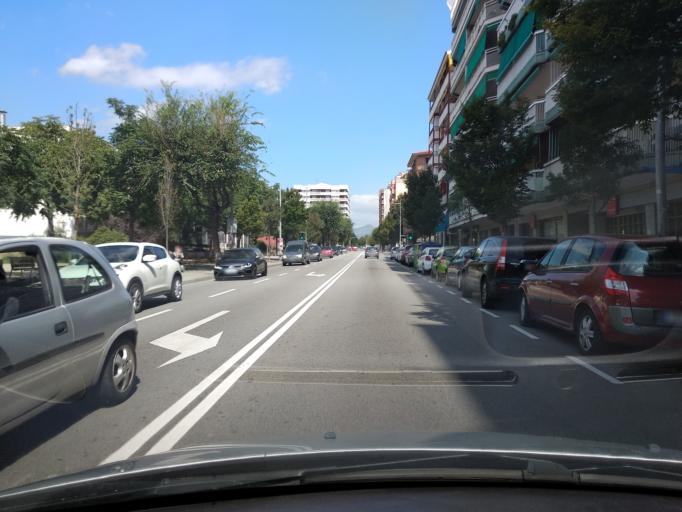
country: ES
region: Catalonia
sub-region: Provincia de Barcelona
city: Granollers
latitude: 41.6077
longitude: 2.2833
